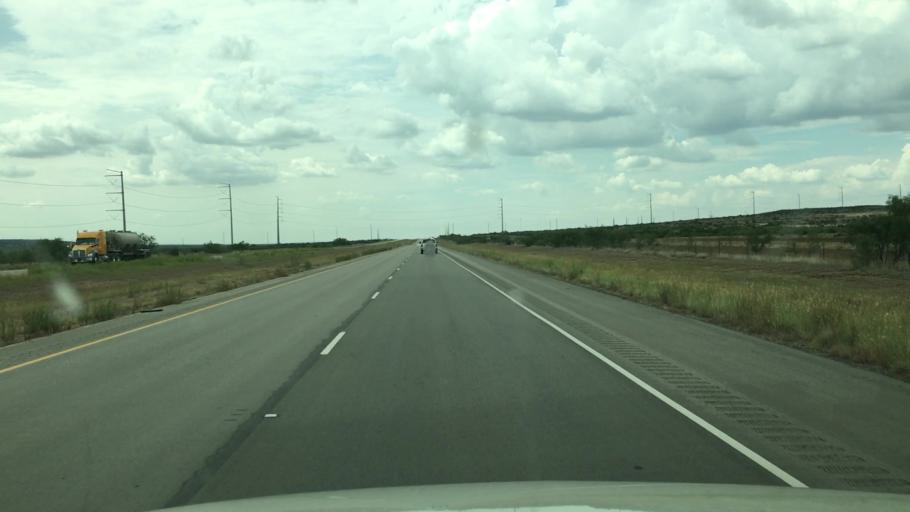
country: US
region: Texas
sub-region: Glasscock County
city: Garden City
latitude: 31.9828
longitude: -101.2576
